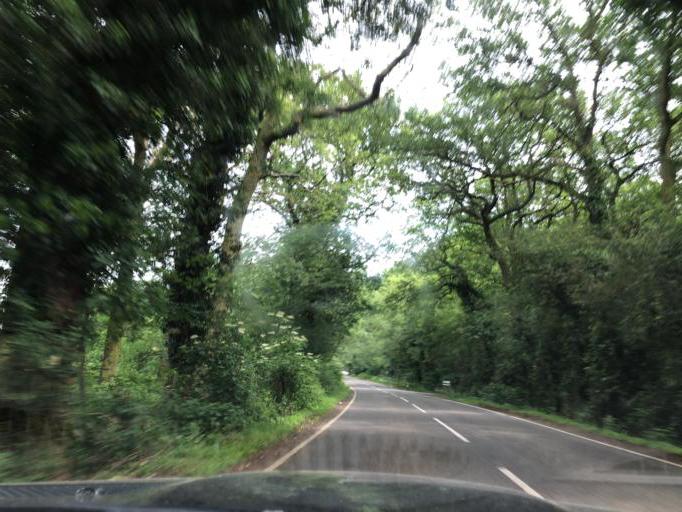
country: GB
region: England
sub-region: Warwickshire
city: Kenilworth
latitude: 52.3236
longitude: -1.5979
